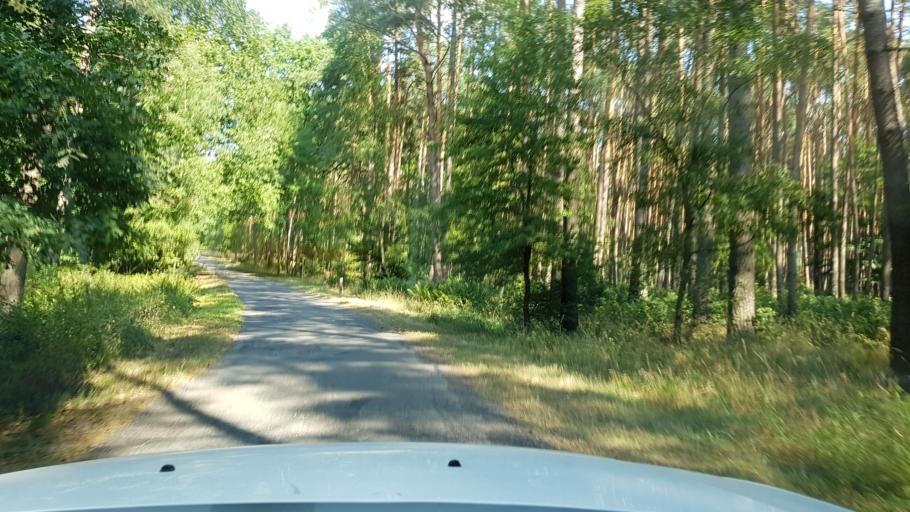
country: PL
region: West Pomeranian Voivodeship
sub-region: Powiat gryfinski
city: Moryn
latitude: 52.8137
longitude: 14.3365
